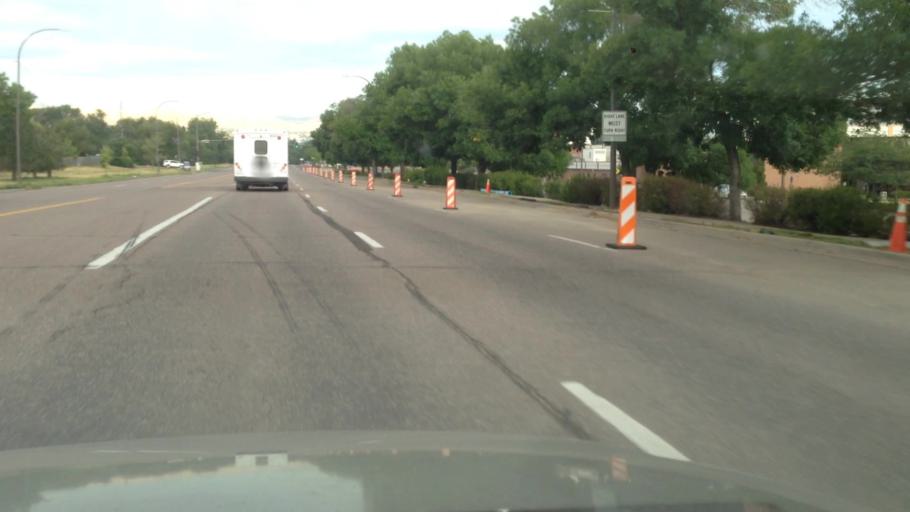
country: US
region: Colorado
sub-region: Jefferson County
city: Lakewood
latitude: 39.7110
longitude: -105.0884
